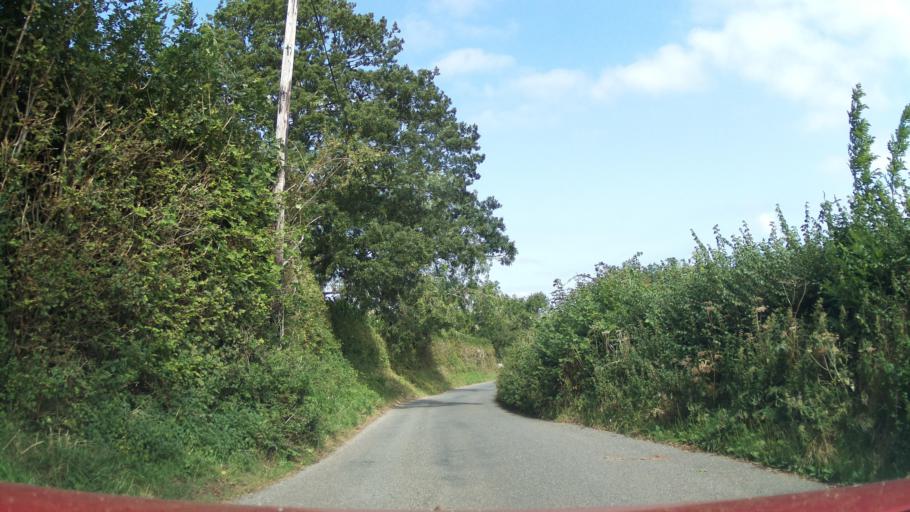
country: GB
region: England
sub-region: Borough of Torbay
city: Paignton
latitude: 50.4019
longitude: -3.6067
